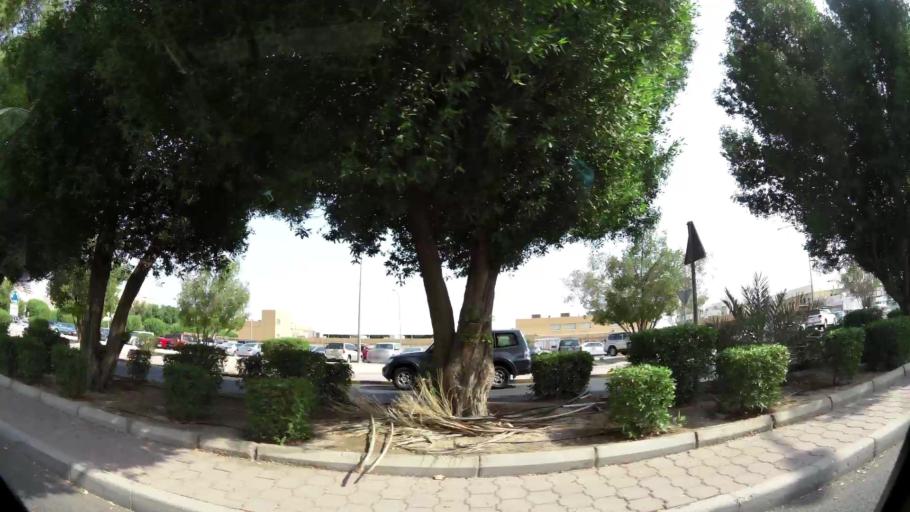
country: KW
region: Muhafazat al Jahra'
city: Al Jahra'
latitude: 29.3321
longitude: 47.6545
